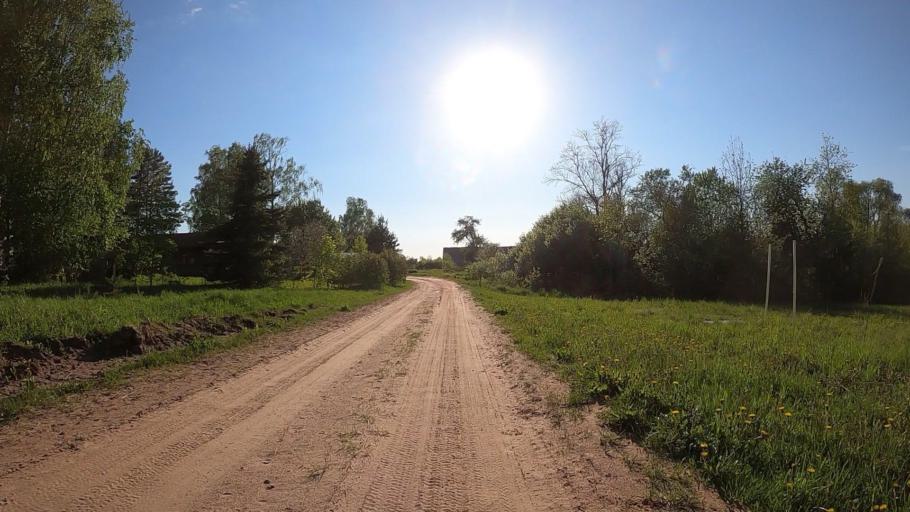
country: LV
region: Baldone
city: Baldone
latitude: 56.7737
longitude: 24.3362
